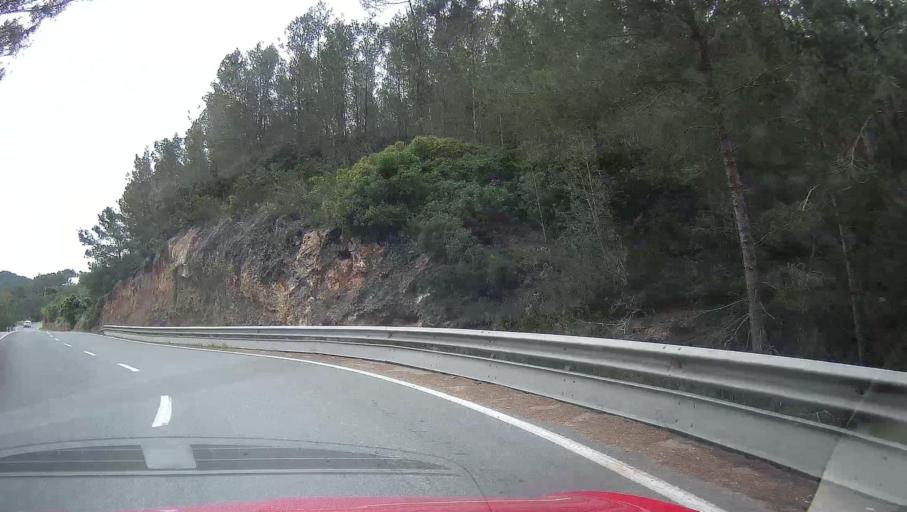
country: ES
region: Balearic Islands
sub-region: Illes Balears
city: Sant Joan de Labritja
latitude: 39.0832
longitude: 1.4952
